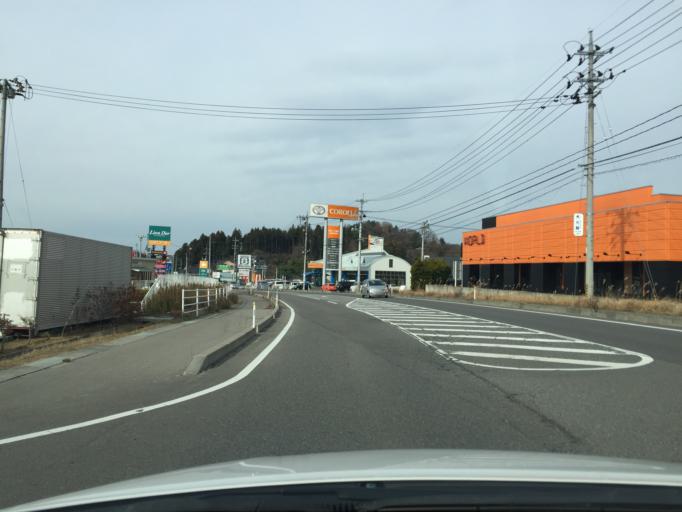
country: JP
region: Fukushima
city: Funehikimachi-funehiki
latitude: 37.4342
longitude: 140.5938
